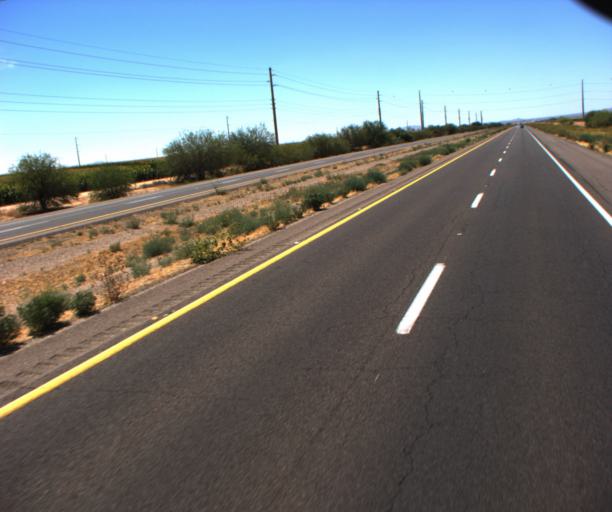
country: US
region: Arizona
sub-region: Pinal County
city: Maricopa
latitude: 32.9702
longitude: -112.0479
